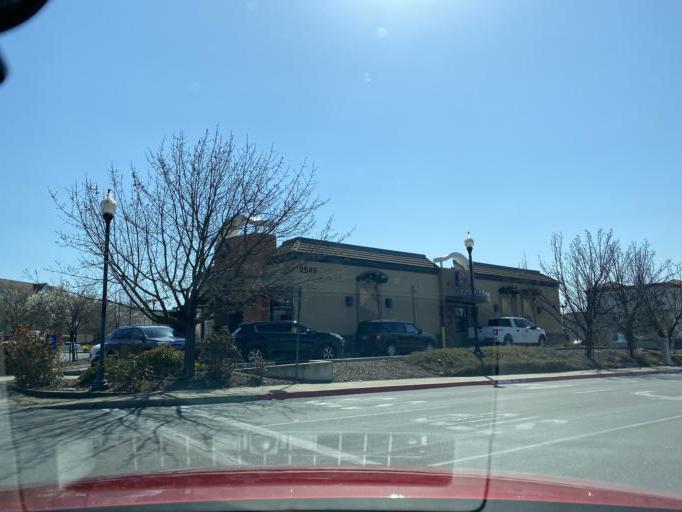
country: US
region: California
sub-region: El Dorado County
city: El Dorado Hills
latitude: 38.6466
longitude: -121.1171
